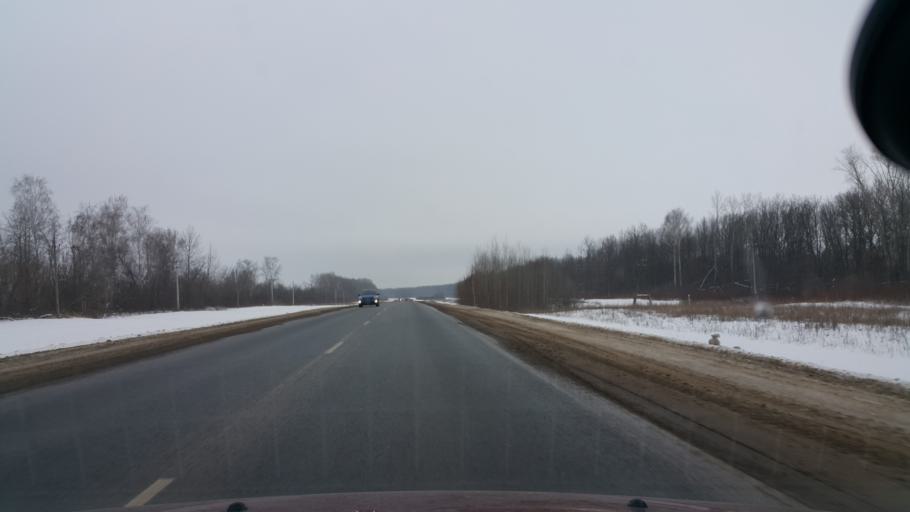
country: RU
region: Tambov
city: Bokino
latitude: 52.6112
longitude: 41.4436
